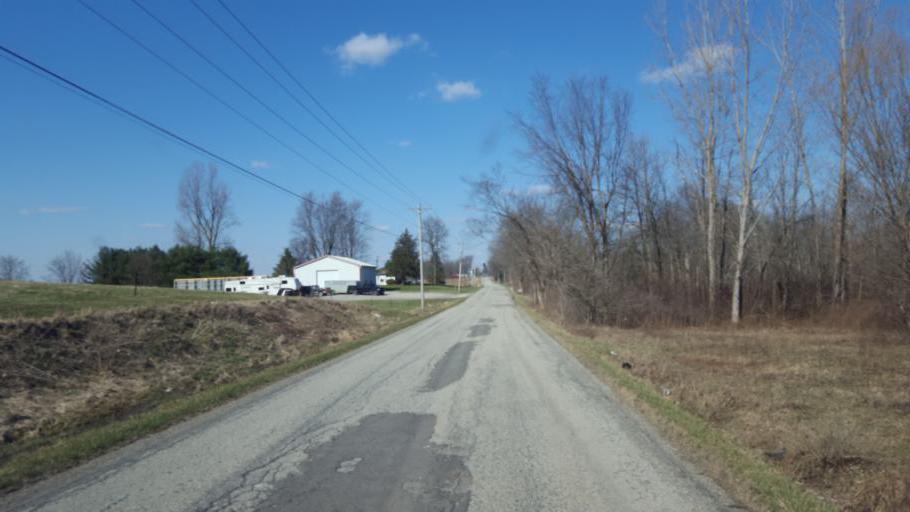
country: US
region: Ohio
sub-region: Morrow County
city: Mount Gilead
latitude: 40.4804
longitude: -82.7548
